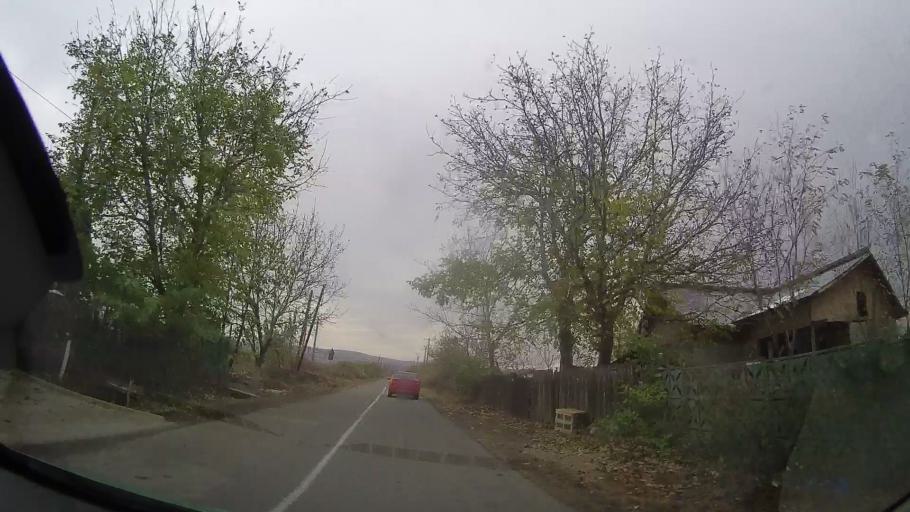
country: RO
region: Prahova
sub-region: Comuna Fantanele
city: Fantanele
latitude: 45.0159
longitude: 26.3802
